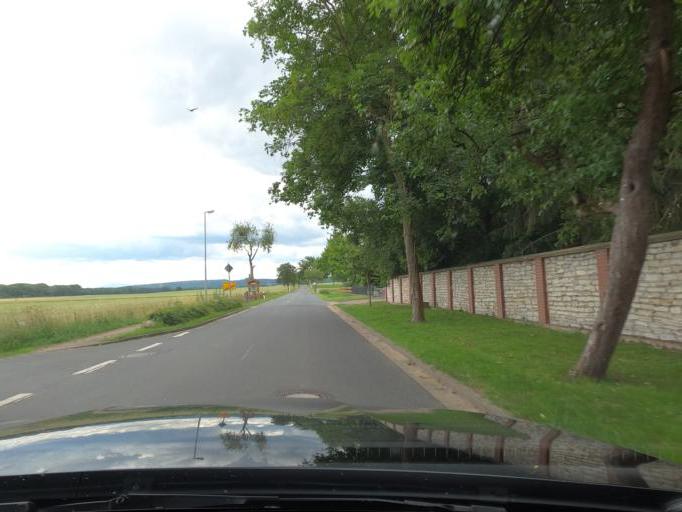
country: DE
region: Lower Saxony
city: Heere
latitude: 52.0616
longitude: 10.2518
